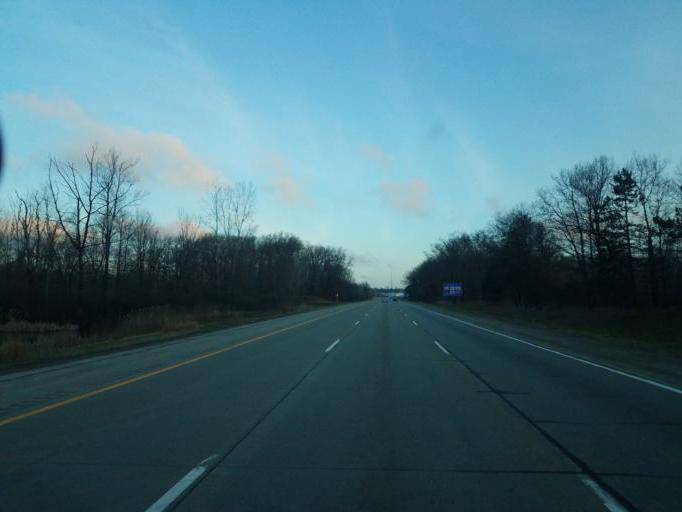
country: US
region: Michigan
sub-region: Livingston County
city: Brighton
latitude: 42.5720
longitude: -83.8460
